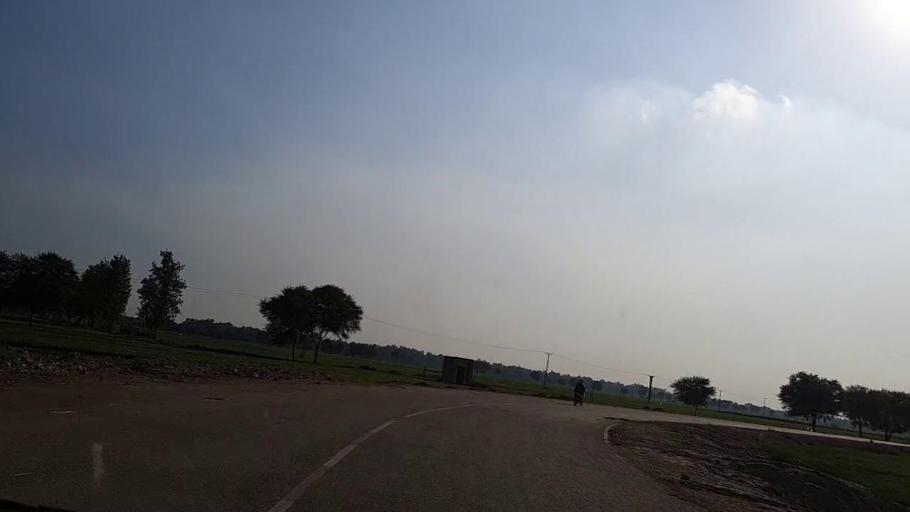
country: PK
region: Sindh
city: Sakrand
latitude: 26.1181
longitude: 68.2498
